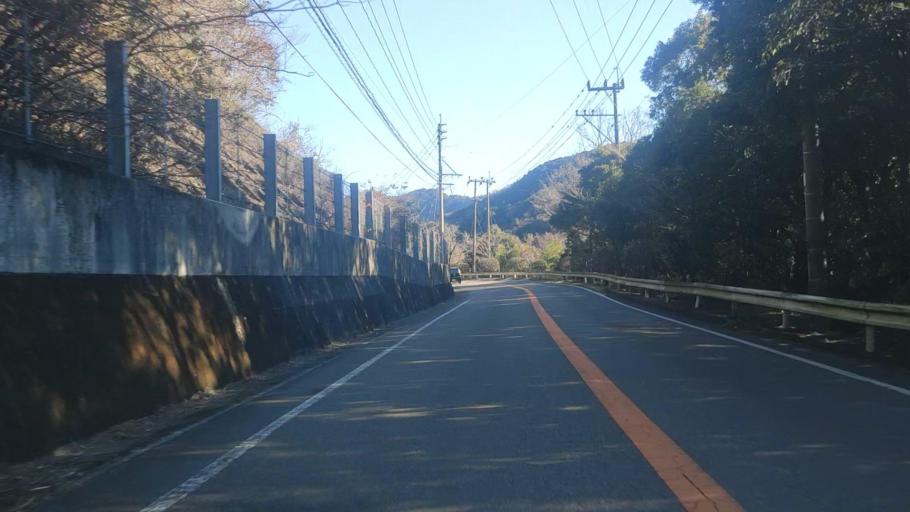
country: JP
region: Miyazaki
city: Nobeoka
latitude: 32.6200
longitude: 131.7049
